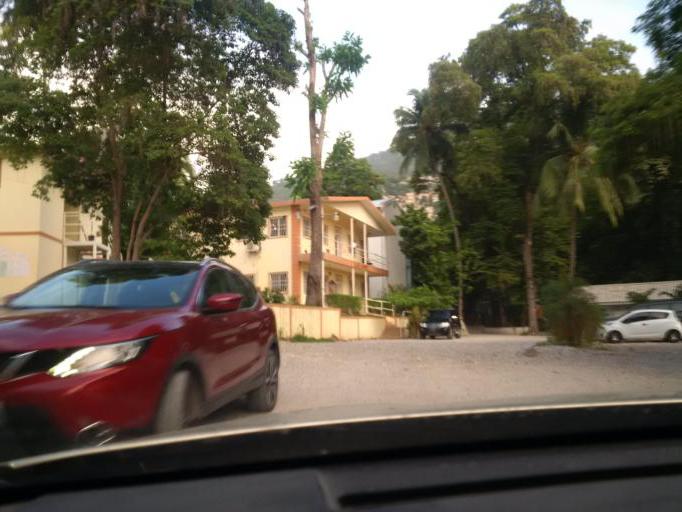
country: HT
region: Ouest
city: Port-au-Prince
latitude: 18.5261
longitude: -72.3218
